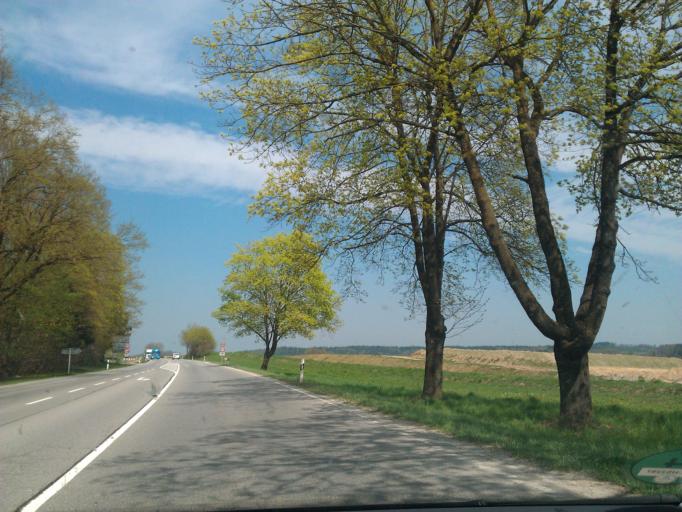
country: DE
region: Bavaria
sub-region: Swabia
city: Obergriesbach
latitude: 48.4026
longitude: 11.0835
